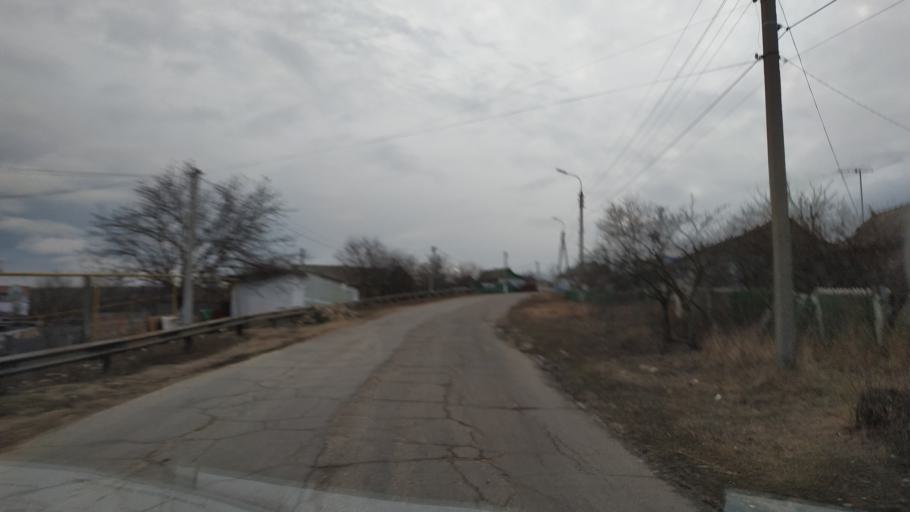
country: MD
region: Causeni
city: Causeni
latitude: 46.6276
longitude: 29.4019
